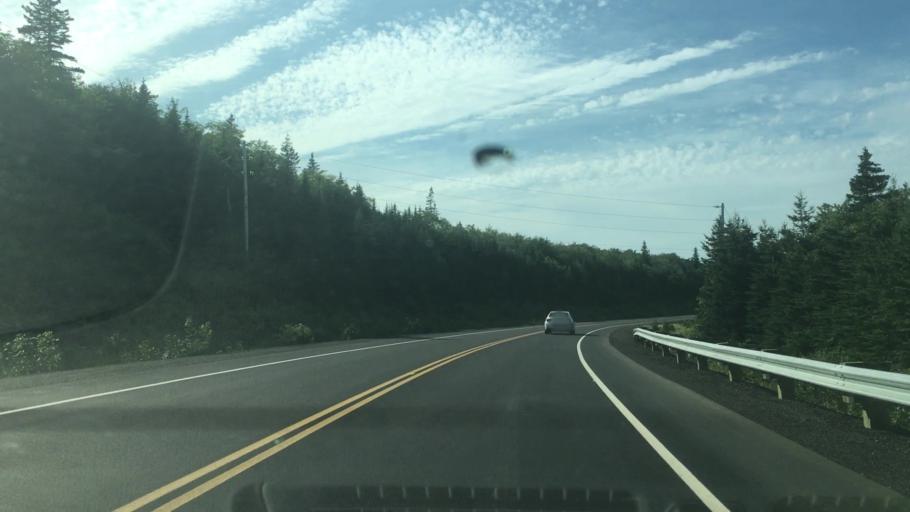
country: CA
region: Nova Scotia
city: Sydney Mines
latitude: 46.8374
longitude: -60.3838
